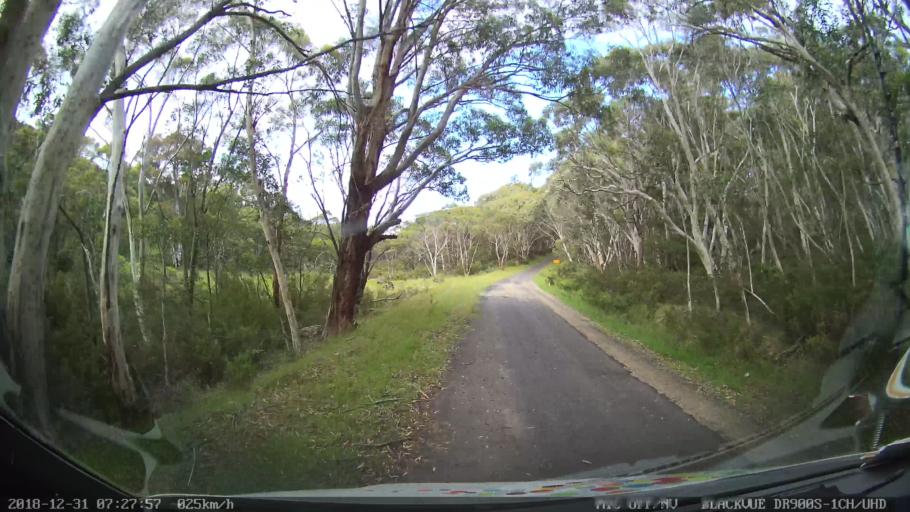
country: AU
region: New South Wales
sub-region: Snowy River
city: Jindabyne
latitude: -36.3223
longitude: 148.4777
